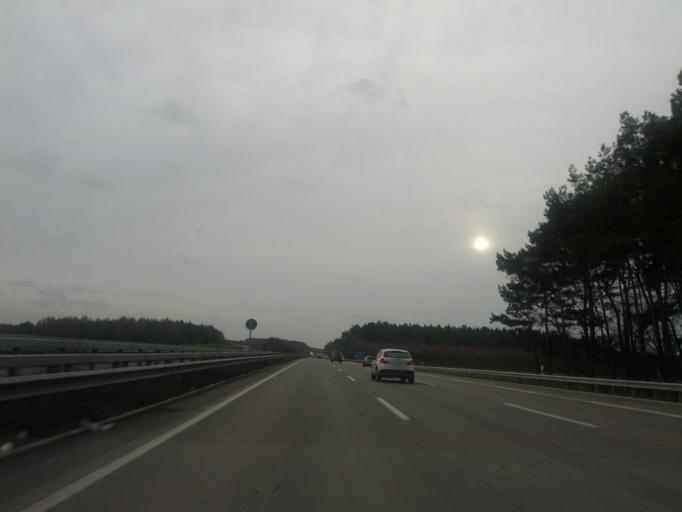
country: DE
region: Lower Saxony
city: Brackel
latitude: 53.3287
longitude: 10.0467
